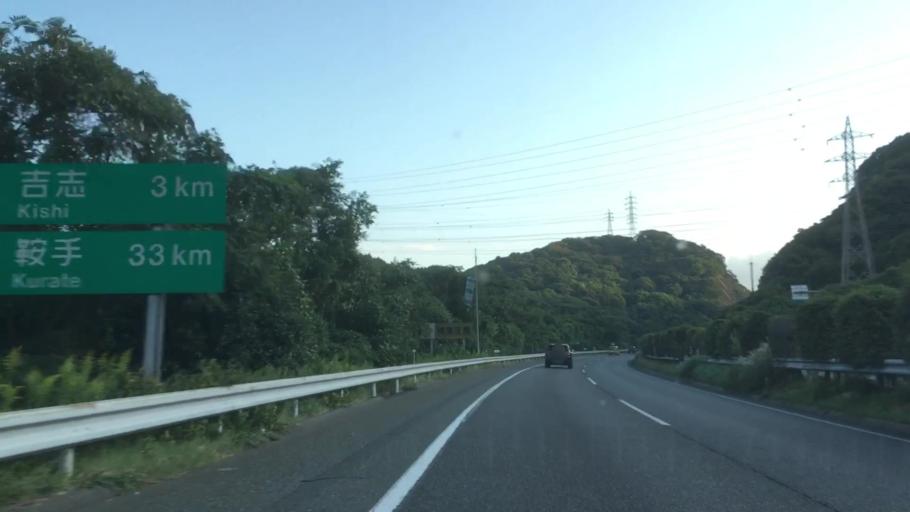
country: JP
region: Yamaguchi
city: Shimonoseki
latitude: 33.8961
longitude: 130.9725
